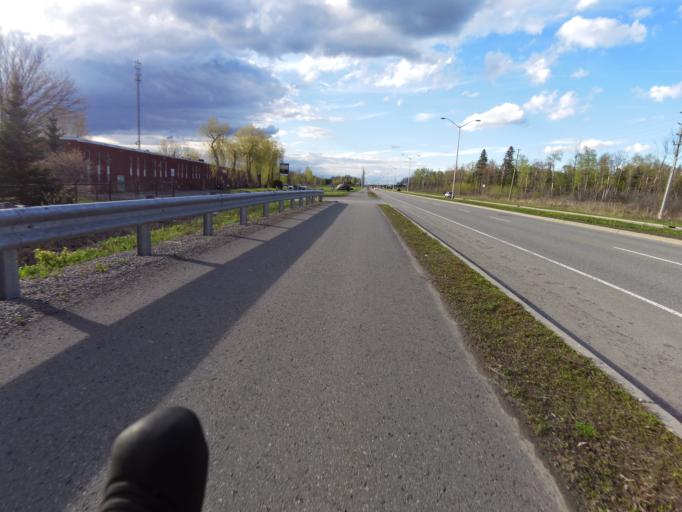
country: CA
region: Ontario
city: Ottawa
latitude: 45.3175
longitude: -75.6875
